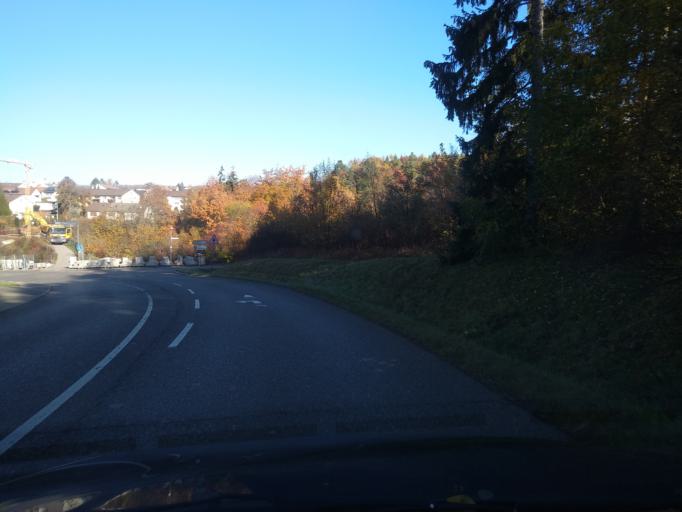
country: DE
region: Baden-Wuerttemberg
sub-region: Karlsruhe Region
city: Calw
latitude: 48.7076
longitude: 8.7669
